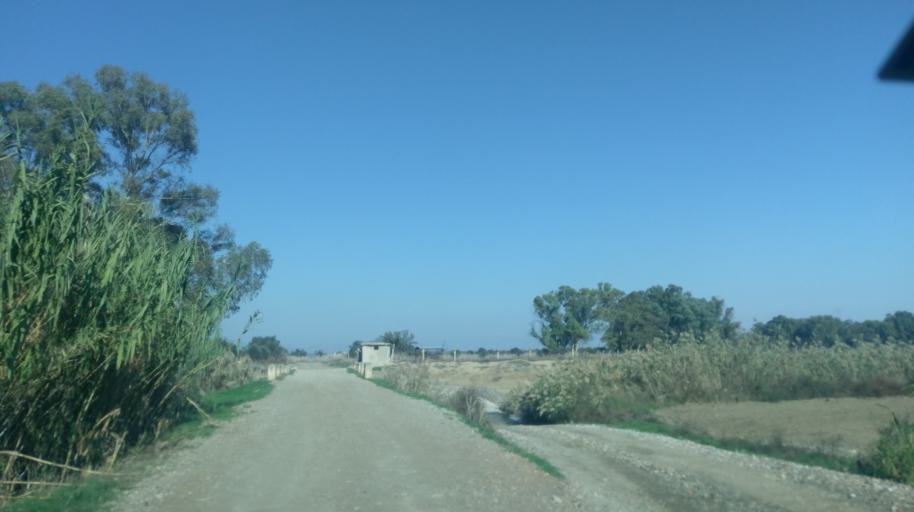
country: CY
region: Larnaka
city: Athienou
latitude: 35.1786
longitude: 33.5530
